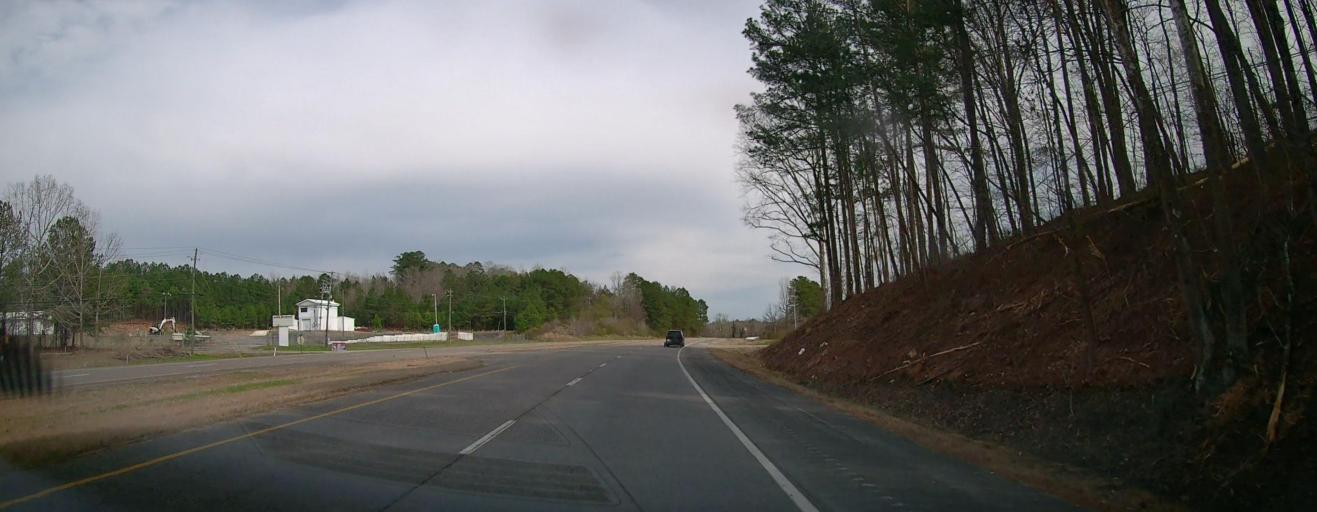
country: US
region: Alabama
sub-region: Walker County
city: Sumiton
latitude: 33.7938
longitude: -87.0972
